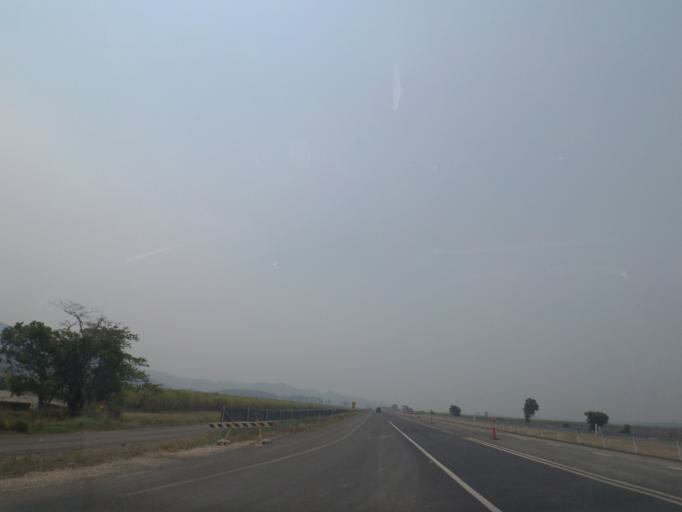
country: AU
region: New South Wales
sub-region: Ballina
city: Ballina
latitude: -28.9010
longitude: 153.4799
